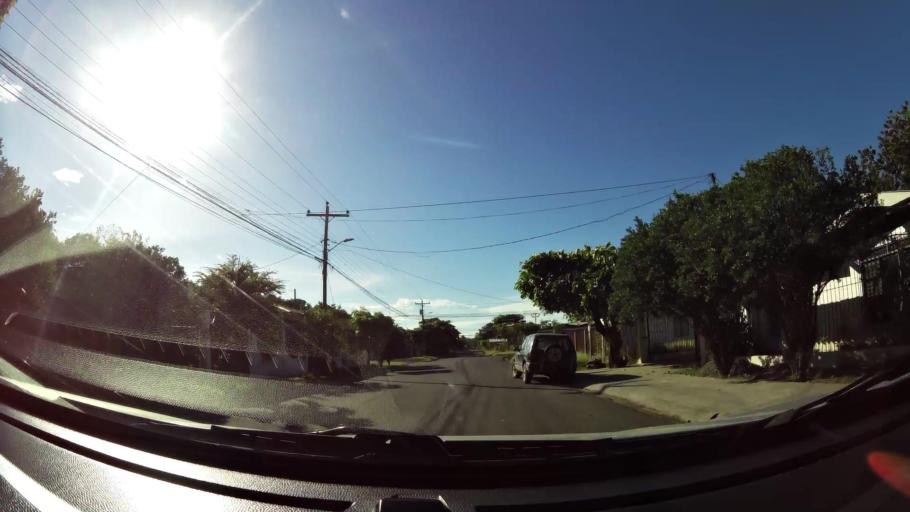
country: CR
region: Guanacaste
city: Belen
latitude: 10.4458
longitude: -85.5521
